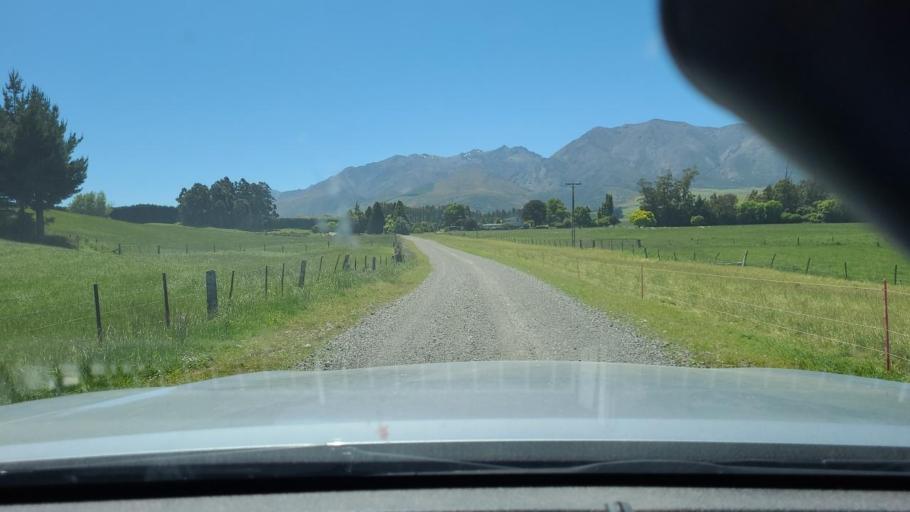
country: NZ
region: Southland
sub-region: Southland District
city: Te Anau
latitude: -45.8375
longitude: 167.7148
